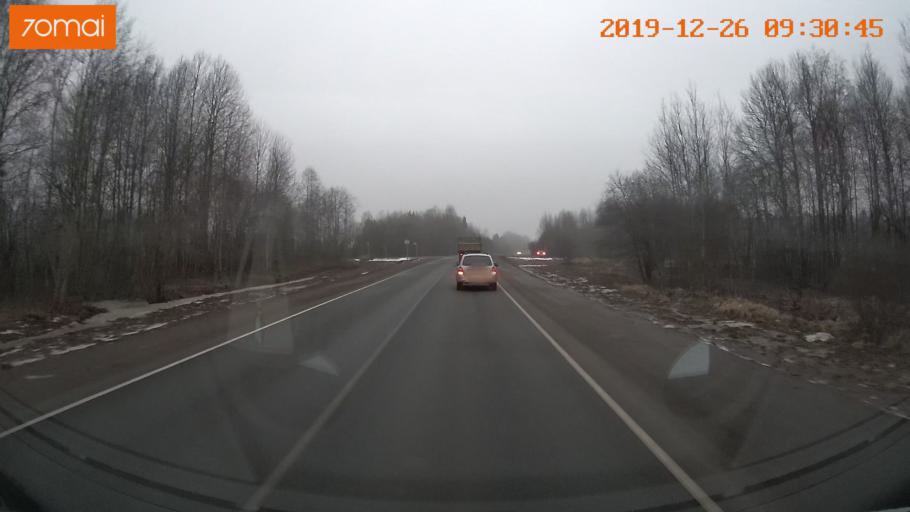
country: RU
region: Vologda
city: Gryazovets
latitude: 59.0631
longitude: 40.1363
